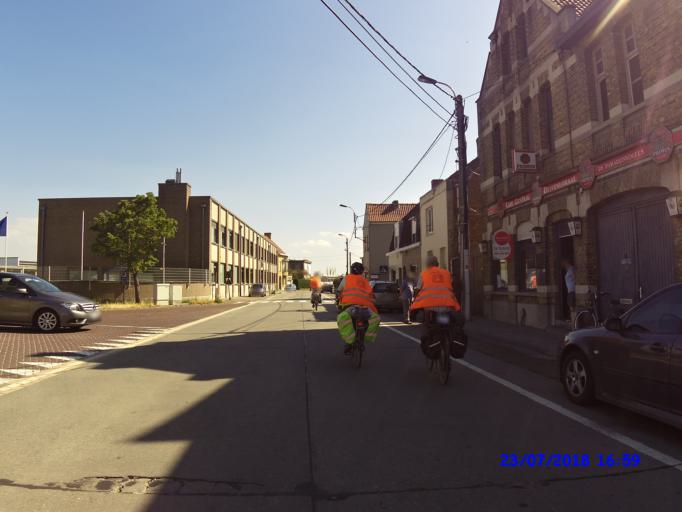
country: BE
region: Flanders
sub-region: Provincie West-Vlaanderen
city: Veurne
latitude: 51.0731
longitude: 2.6716
